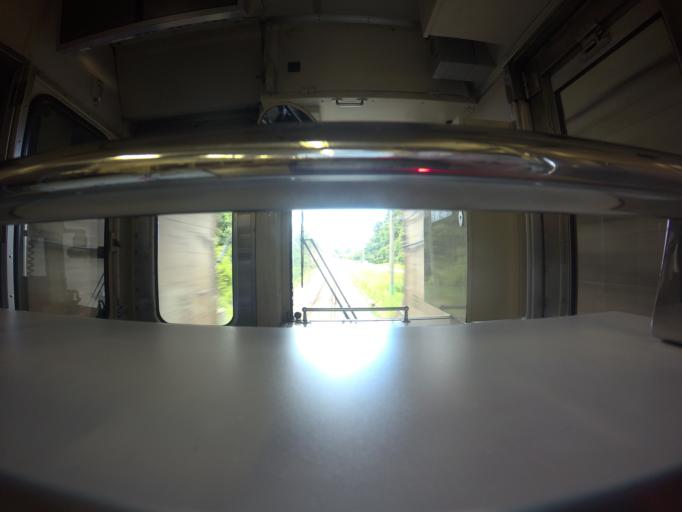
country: JP
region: Fukushima
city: Namie
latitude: 37.5324
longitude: 140.9854
